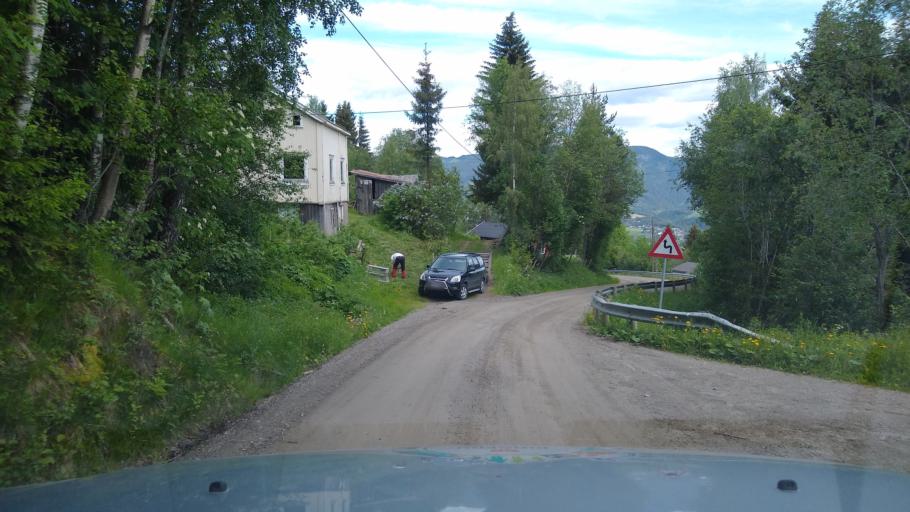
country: NO
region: Oppland
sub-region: Ringebu
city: Ringebu
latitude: 61.5075
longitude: 10.1355
